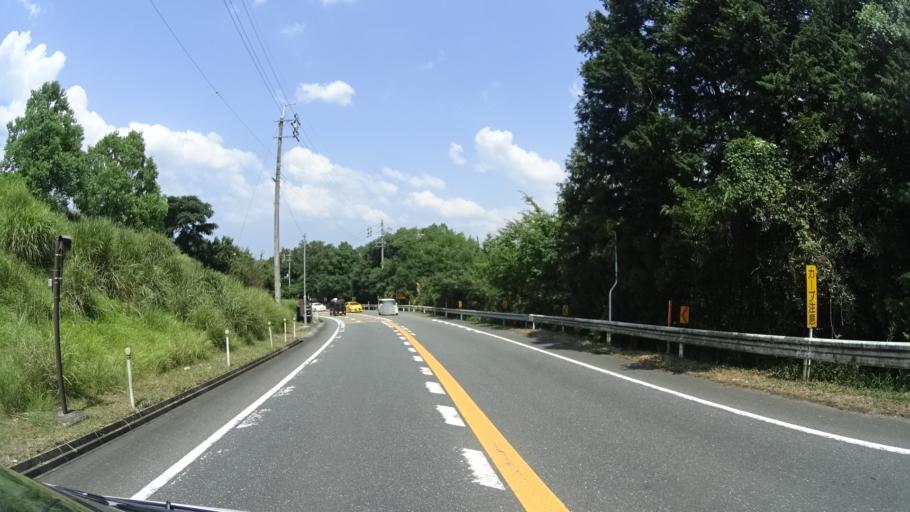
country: JP
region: Kyoto
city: Fukuchiyama
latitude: 35.2684
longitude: 135.1462
